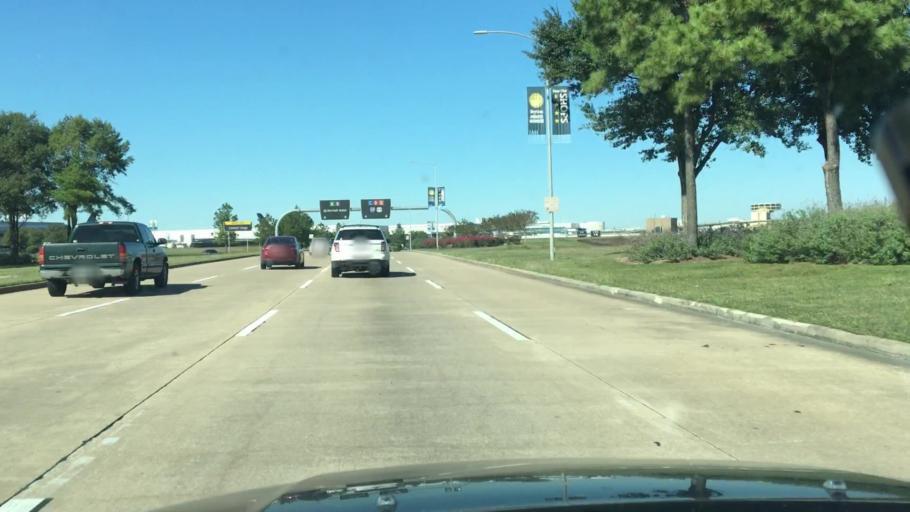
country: US
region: Texas
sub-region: Harris County
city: Aldine
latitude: 29.9744
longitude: -95.3413
